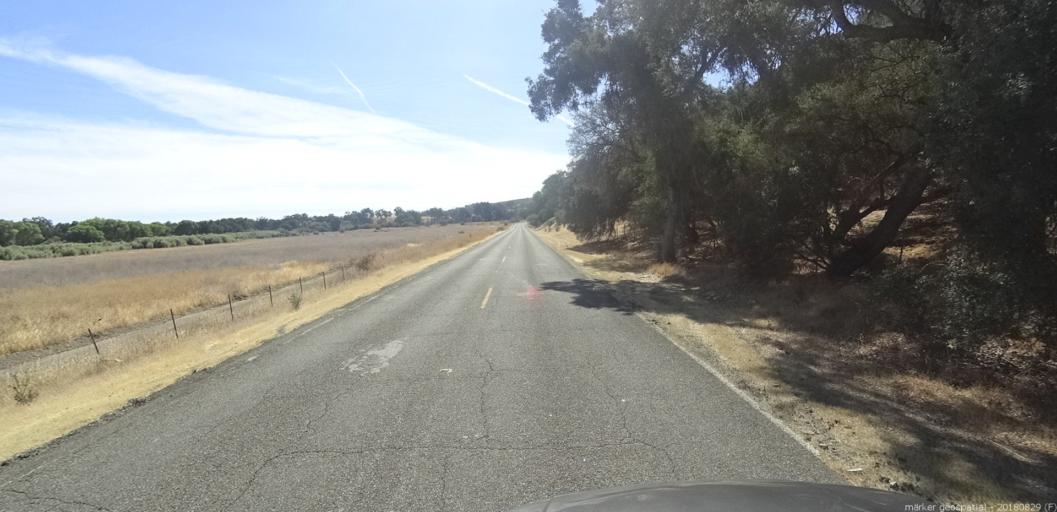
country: US
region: California
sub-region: San Luis Obispo County
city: Lake Nacimiento
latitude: 35.8883
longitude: -121.0724
